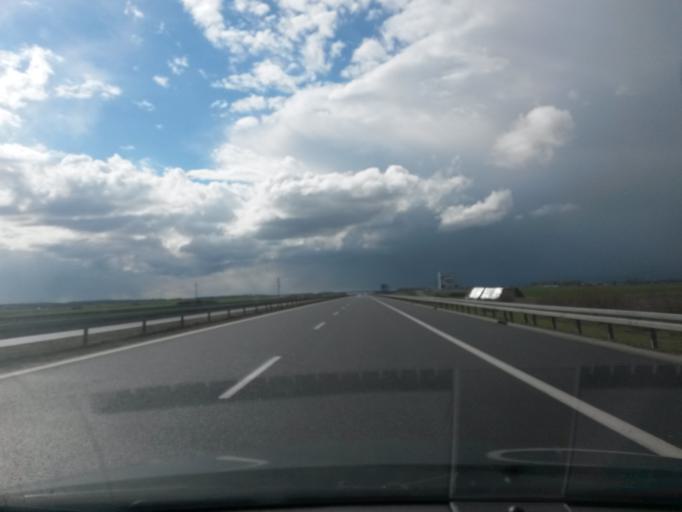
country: PL
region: Greater Poland Voivodeship
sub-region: Powiat wrzesinski
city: Nekla
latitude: 52.3188
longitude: 17.4595
